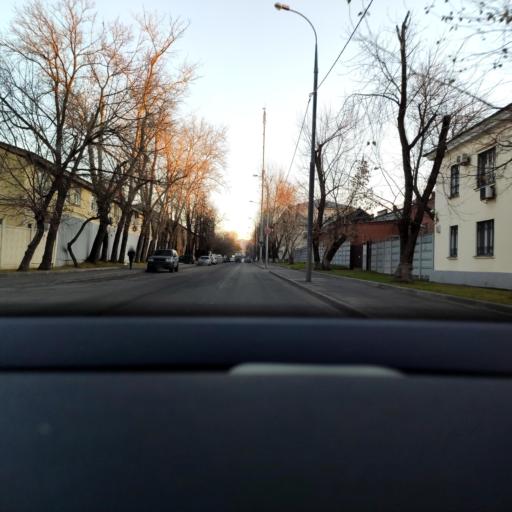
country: RU
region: Moscow
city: Ryazanskiy
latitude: 55.7201
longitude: 37.7538
